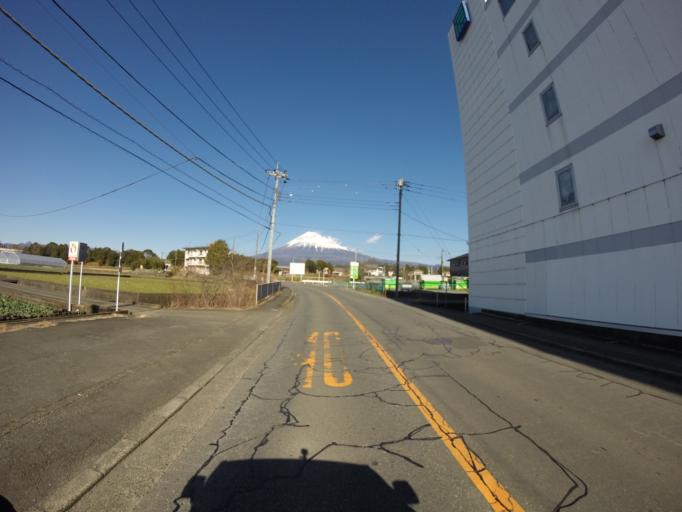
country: JP
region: Shizuoka
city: Fuji
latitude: 35.1748
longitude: 138.6569
